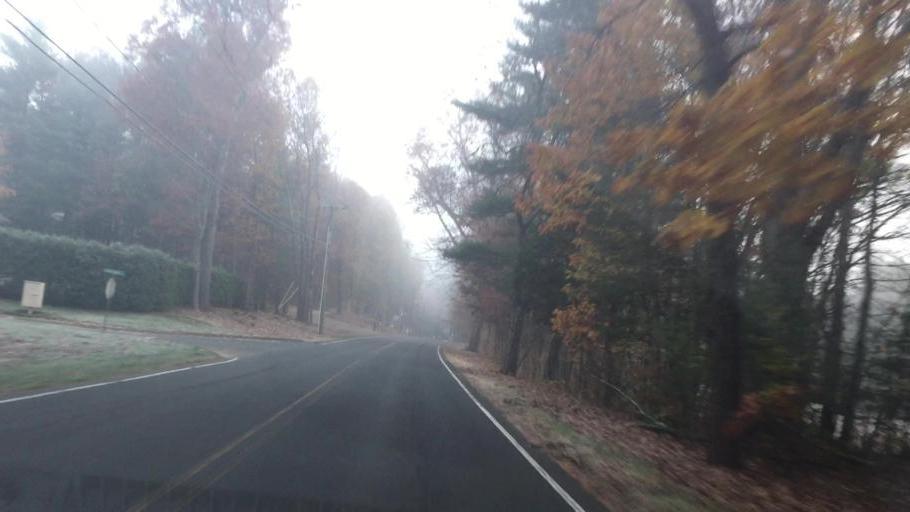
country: US
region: Massachusetts
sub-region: Hampshire County
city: Southampton
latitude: 42.2206
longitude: -72.6891
